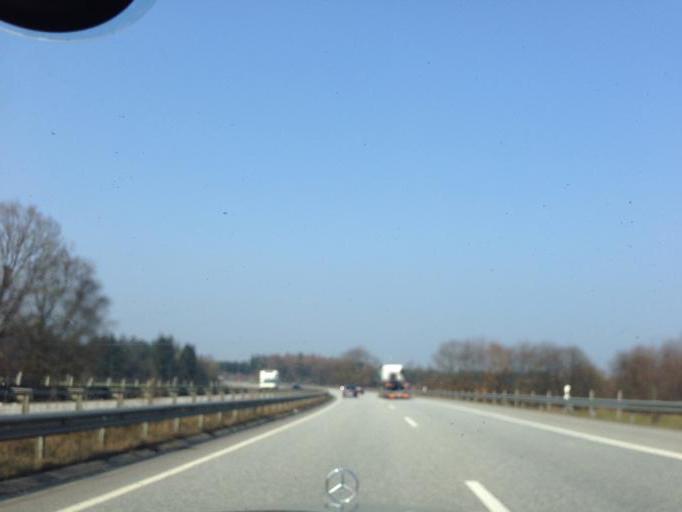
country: DE
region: Schleswig-Holstein
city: Daldorf
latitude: 54.0239
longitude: 10.2450
